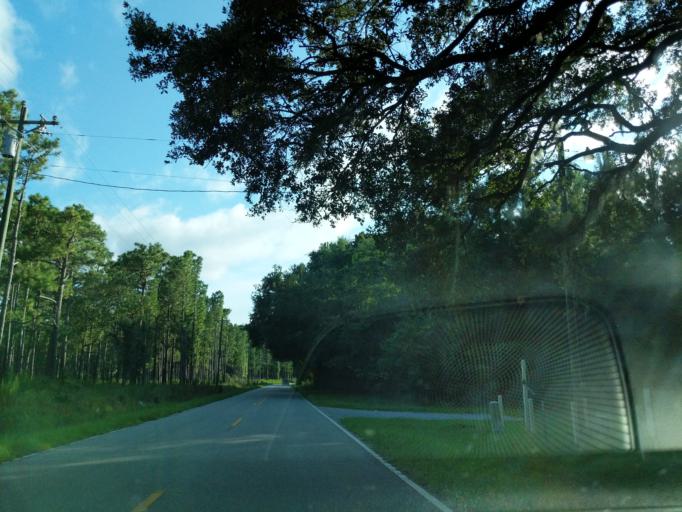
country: US
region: South Carolina
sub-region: Charleston County
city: Awendaw
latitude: 33.1424
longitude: -79.4209
